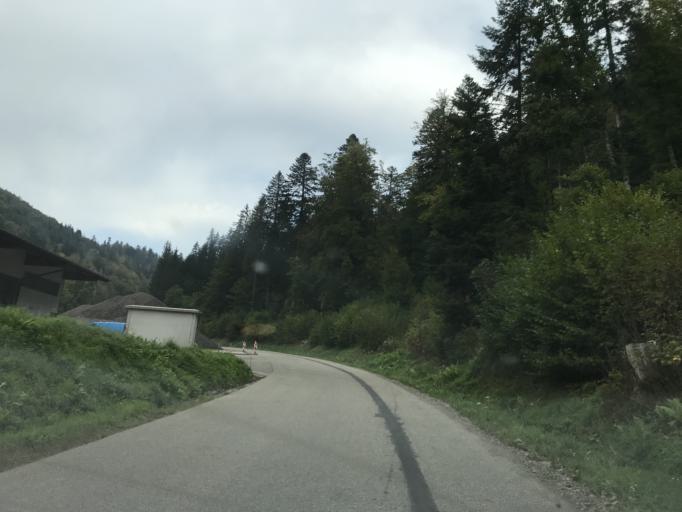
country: DE
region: Baden-Wuerttemberg
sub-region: Freiburg Region
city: Todtmoos
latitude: 47.7029
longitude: 7.9888
